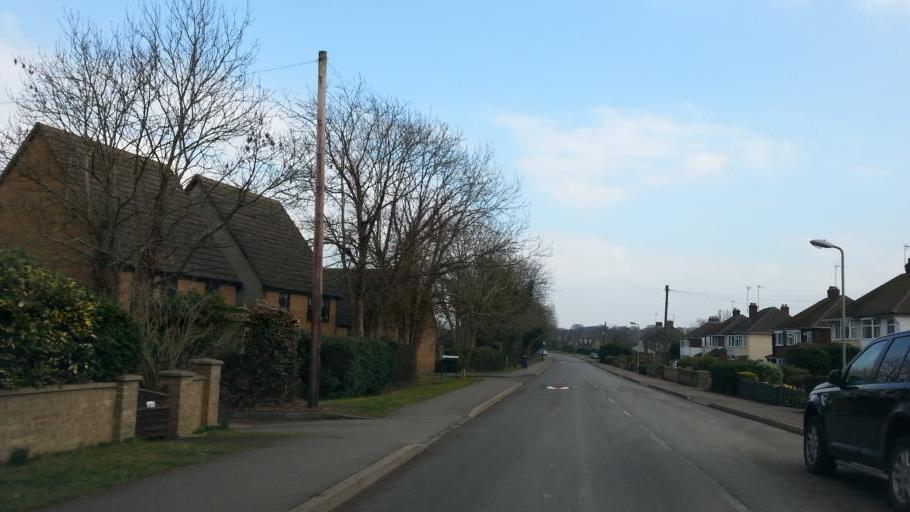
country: GB
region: England
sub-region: Northamptonshire
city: Corby
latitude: 52.4954
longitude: -0.6424
